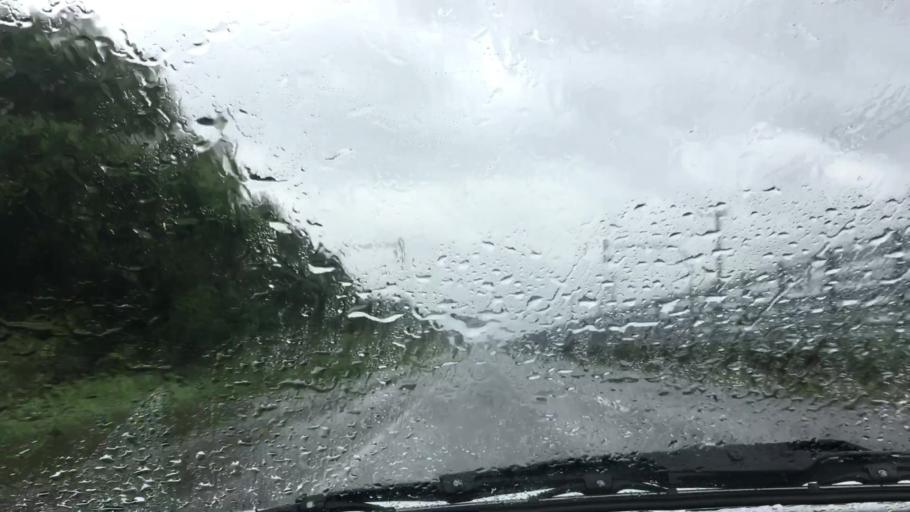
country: JP
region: Hokkaido
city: Nanae
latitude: 42.3115
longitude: 140.2733
